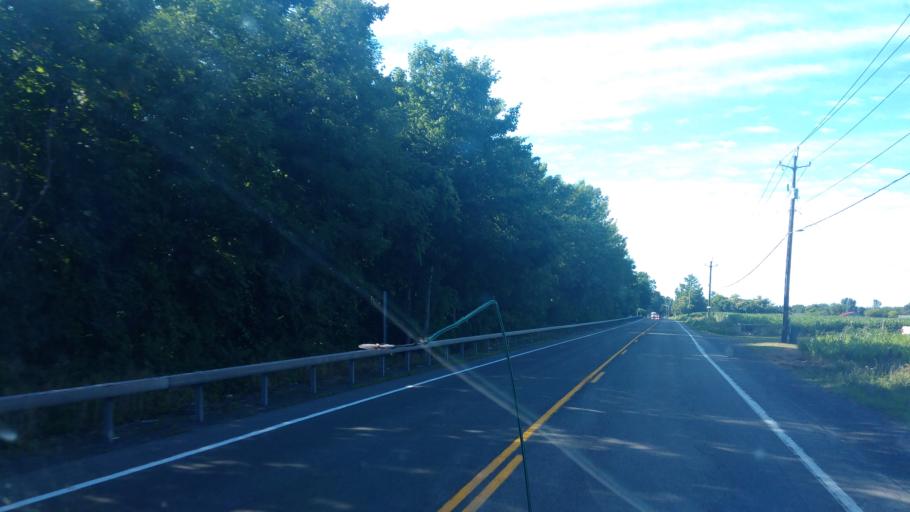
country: US
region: New York
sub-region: Wayne County
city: Lyons
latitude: 43.0403
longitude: -76.9932
